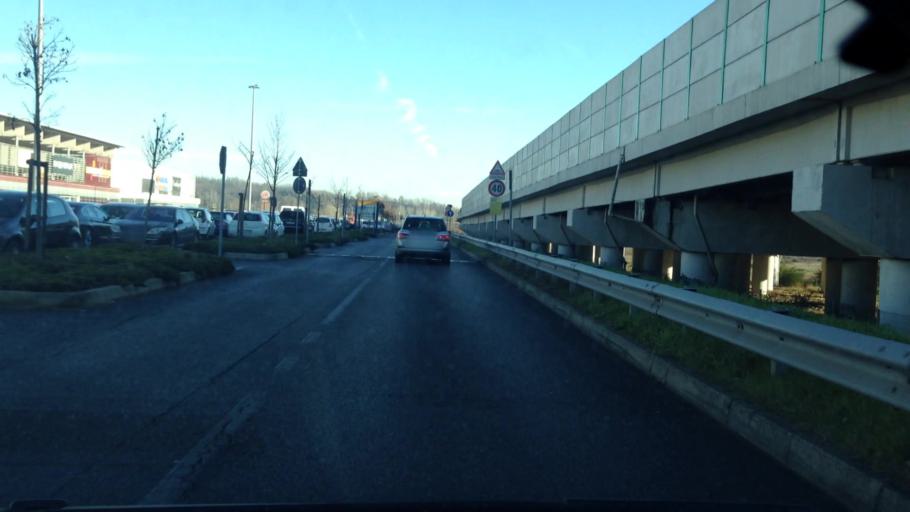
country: IT
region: Piedmont
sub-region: Provincia di Asti
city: Asti
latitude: 44.9147
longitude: 8.2232
